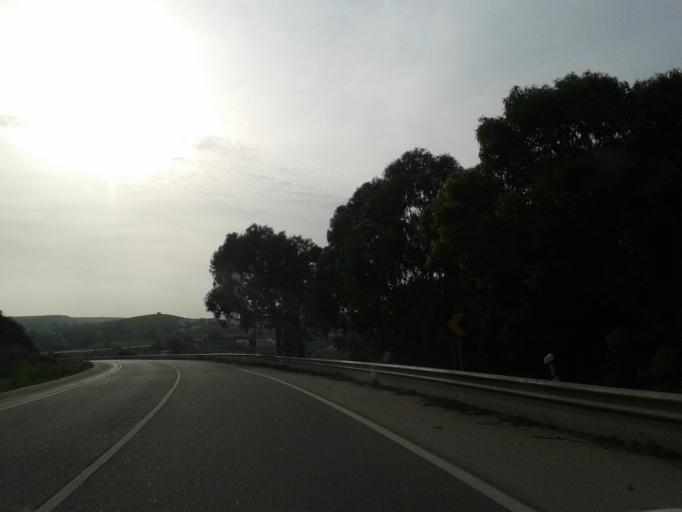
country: PT
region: Faro
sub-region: Vila do Bispo
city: Vila do Bispo
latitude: 37.0781
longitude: -8.8425
